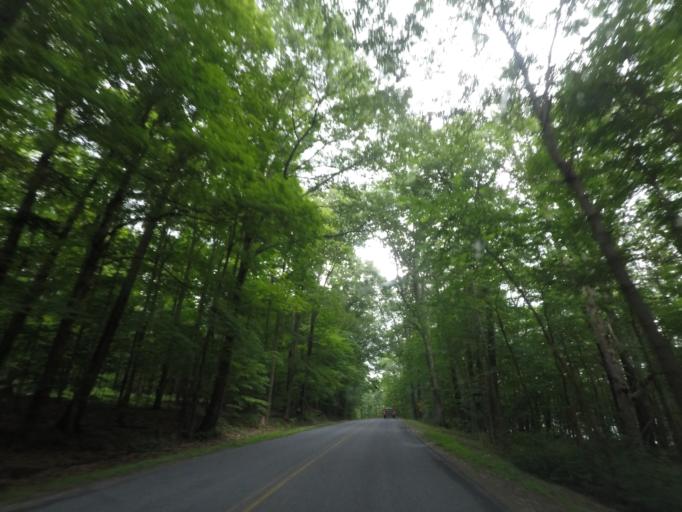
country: US
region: New York
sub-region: Saratoga County
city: Stillwater
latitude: 42.8440
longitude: -73.5377
